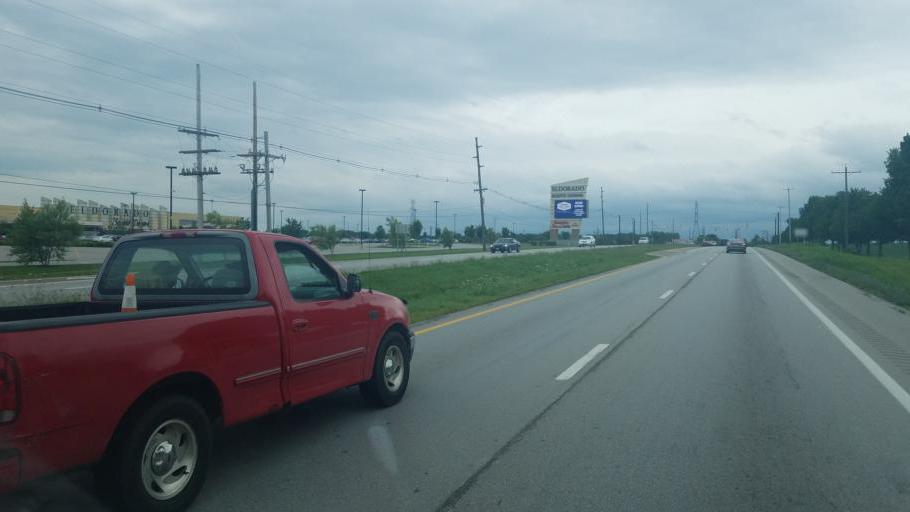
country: US
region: Ohio
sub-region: Franklin County
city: Obetz
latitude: 39.8411
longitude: -83.0009
